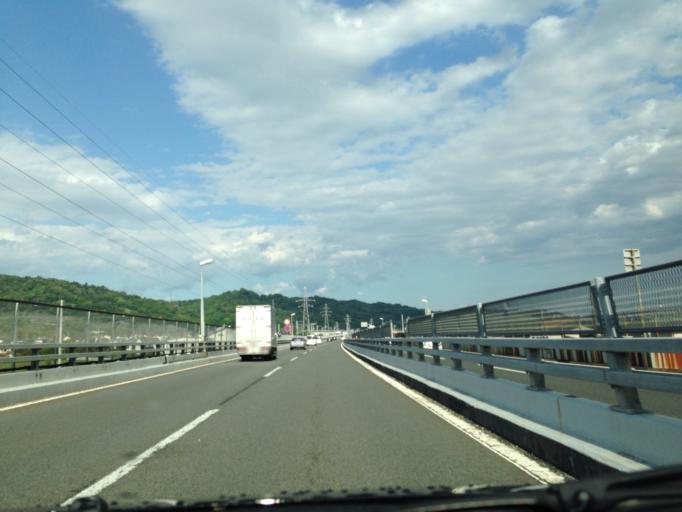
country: JP
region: Kanagawa
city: Odawara
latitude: 35.2906
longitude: 139.1813
